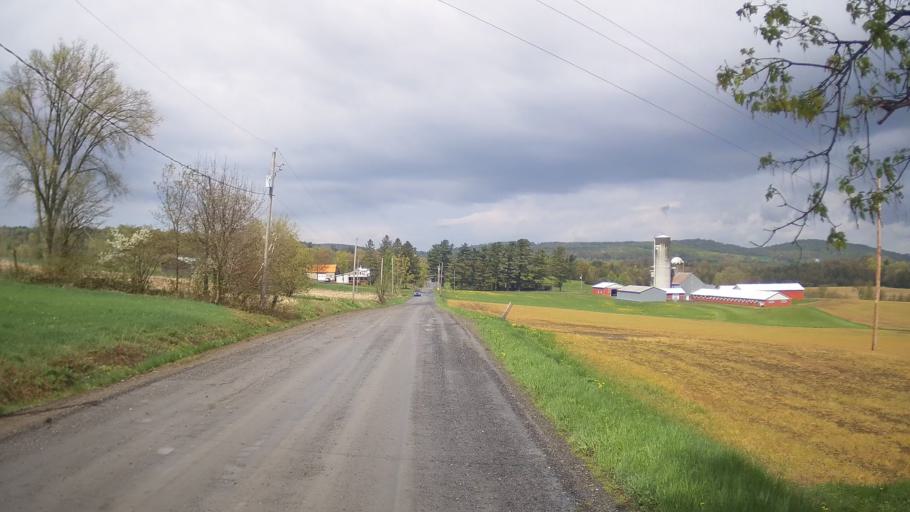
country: CA
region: Quebec
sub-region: Monteregie
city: Cowansville
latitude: 45.1734
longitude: -72.6693
